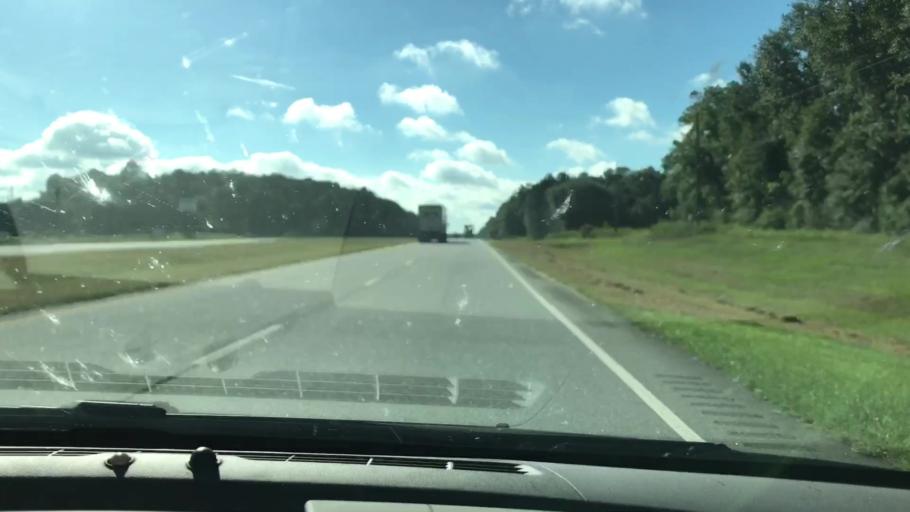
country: US
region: Georgia
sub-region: Dougherty County
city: Albany
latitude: 31.5683
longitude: -84.0212
